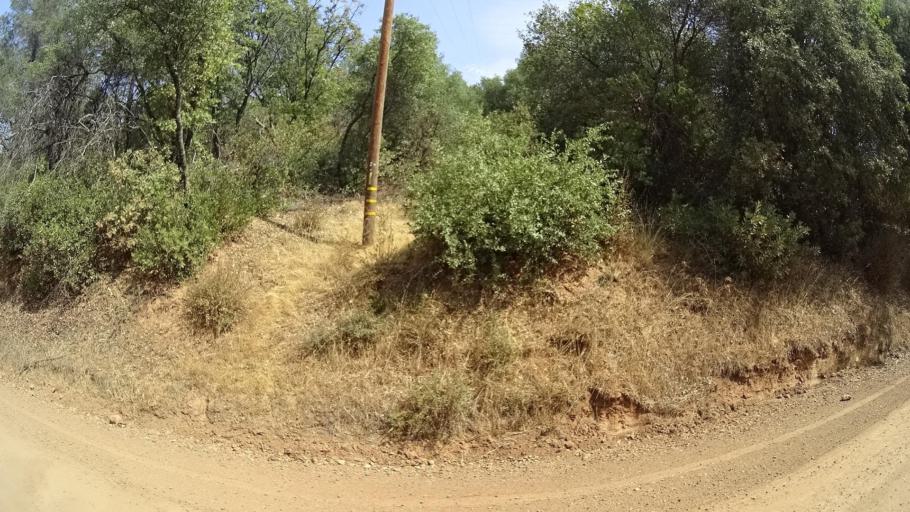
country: US
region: California
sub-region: Mariposa County
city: Midpines
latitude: 37.6946
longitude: -120.1174
